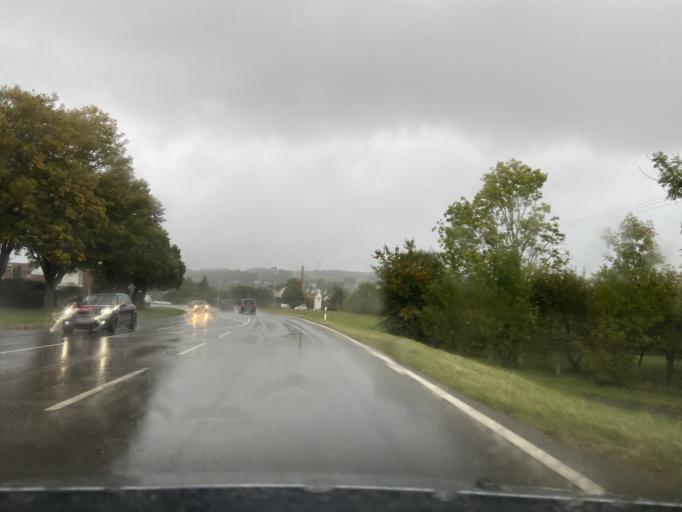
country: DE
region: Baden-Wuerttemberg
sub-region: Tuebingen Region
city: Scheer
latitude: 48.0669
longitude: 9.2974
